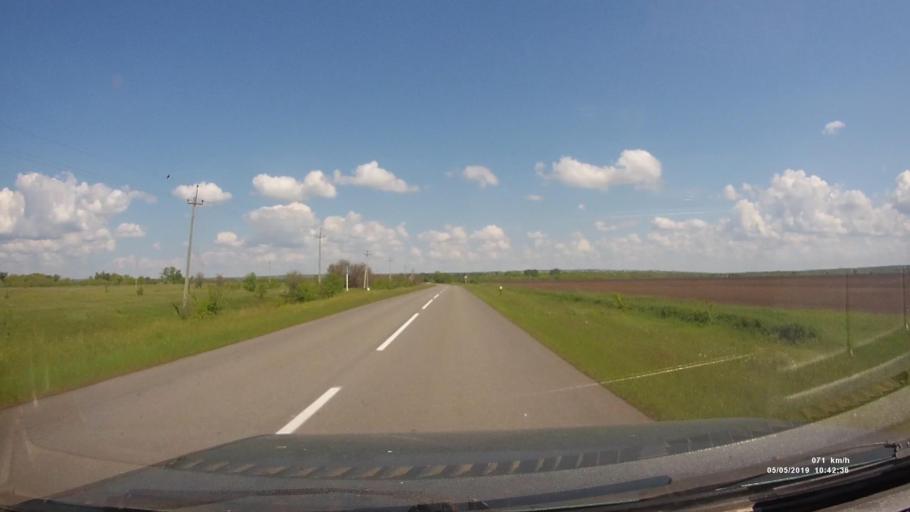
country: RU
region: Rostov
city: Ust'-Donetskiy
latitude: 47.6009
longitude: 40.8386
